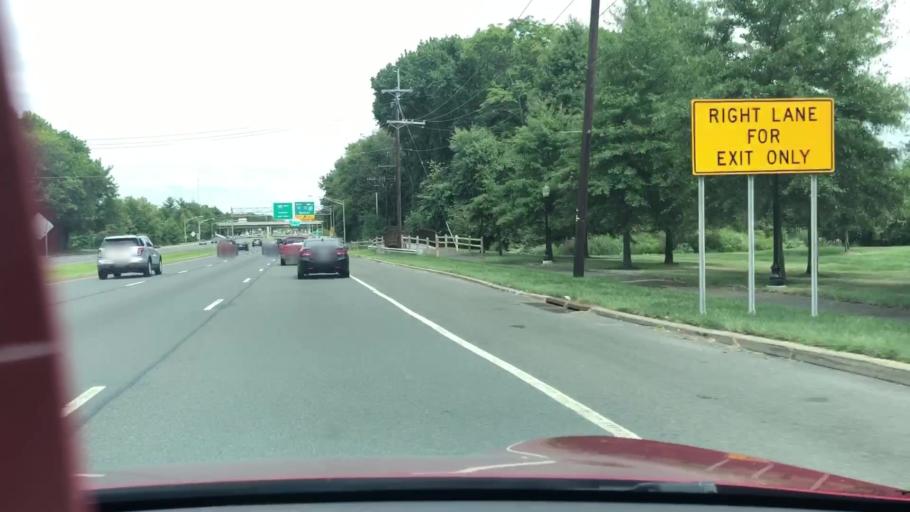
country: US
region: New Jersey
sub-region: Mercer County
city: Robbinsville
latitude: 40.1988
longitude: -74.6385
